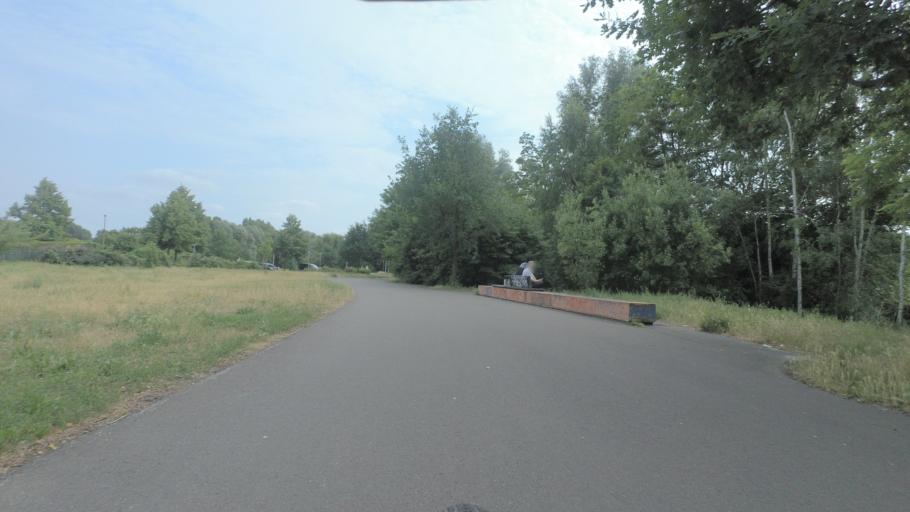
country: DE
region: Berlin
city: Plaenterwald
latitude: 52.4741
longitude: 13.4701
